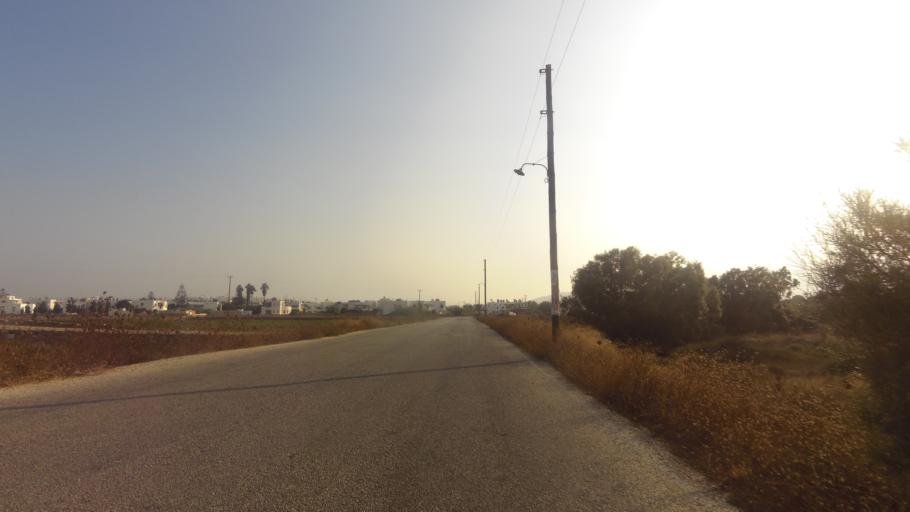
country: GR
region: South Aegean
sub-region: Nomos Kykladon
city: Antiparos
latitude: 37.0370
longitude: 25.0802
